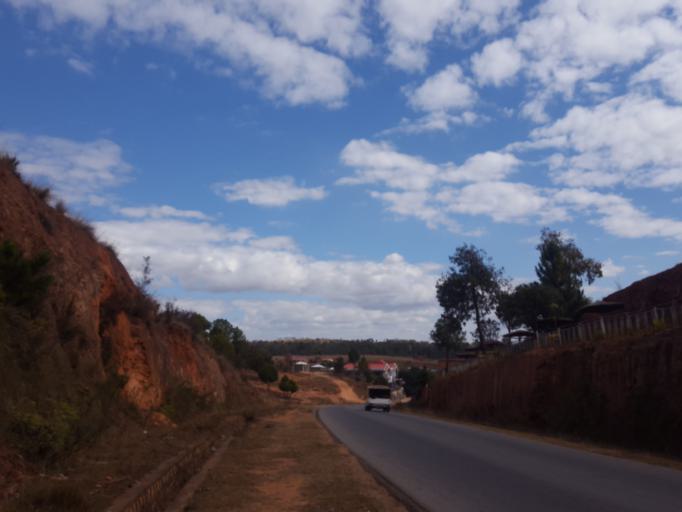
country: MG
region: Analamanga
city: Antananarivo
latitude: -18.9545
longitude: 47.3592
